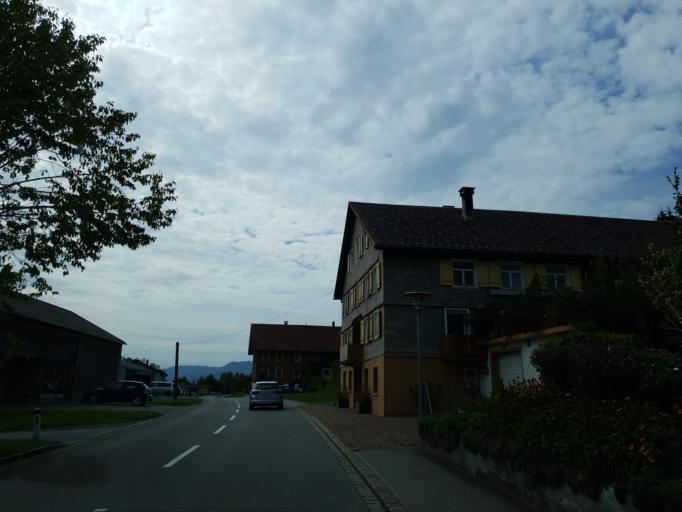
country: AT
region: Vorarlberg
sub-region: Politischer Bezirk Bregenz
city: Doren
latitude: 47.4948
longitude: 9.8881
